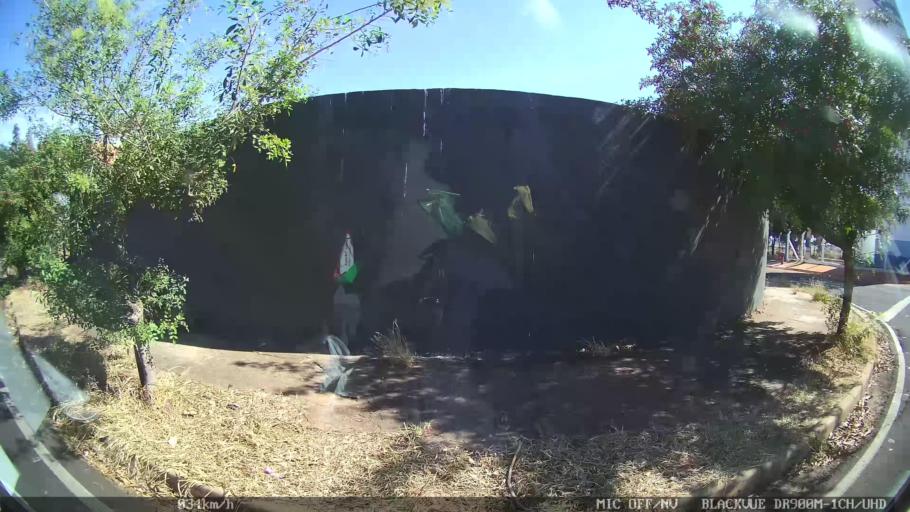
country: BR
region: Sao Paulo
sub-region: Sao Jose Do Rio Preto
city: Sao Jose do Rio Preto
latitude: -20.7701
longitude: -49.4130
